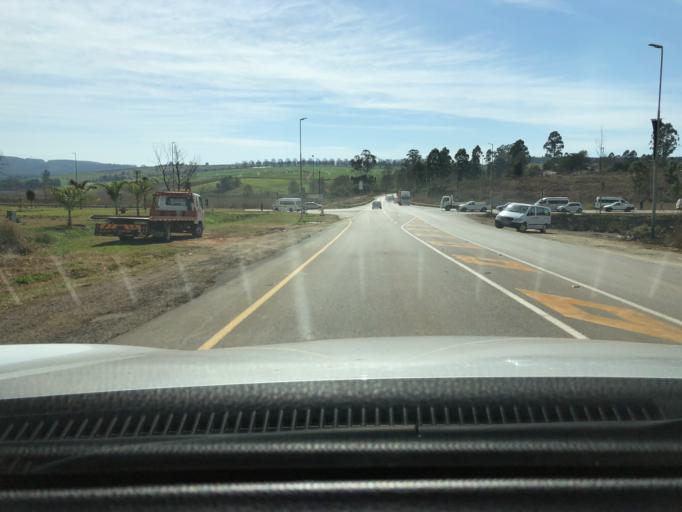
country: ZA
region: KwaZulu-Natal
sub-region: Sisonke District Municipality
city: Ixopo
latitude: -30.1460
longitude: 30.0700
